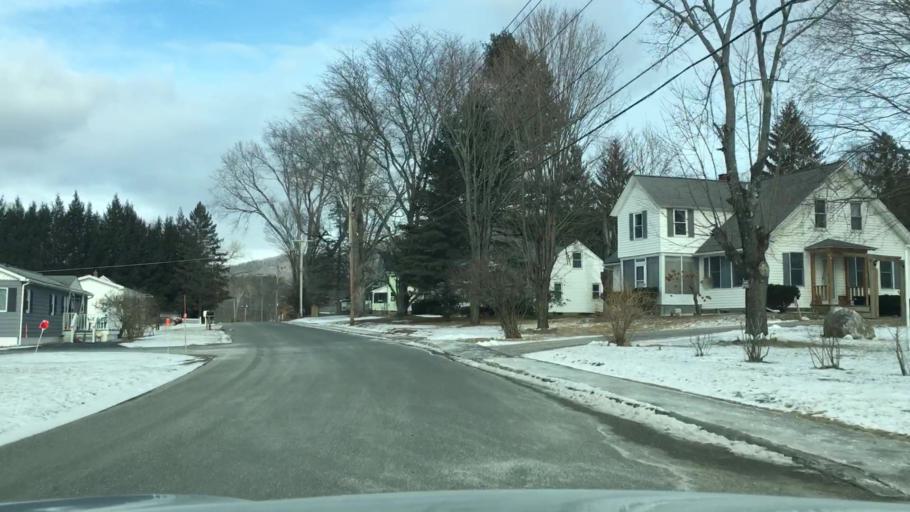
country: US
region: Massachusetts
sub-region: Berkshire County
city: Lee
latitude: 42.3281
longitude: -73.2381
